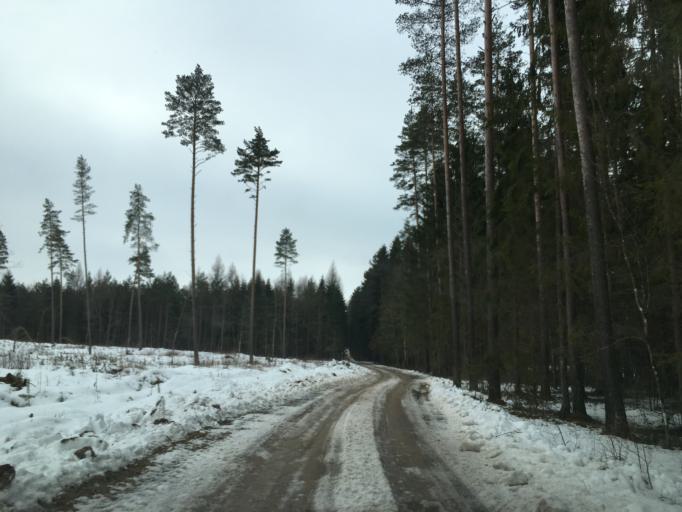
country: EE
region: Tartu
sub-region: Elva linn
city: Elva
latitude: 58.0877
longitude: 26.1985
